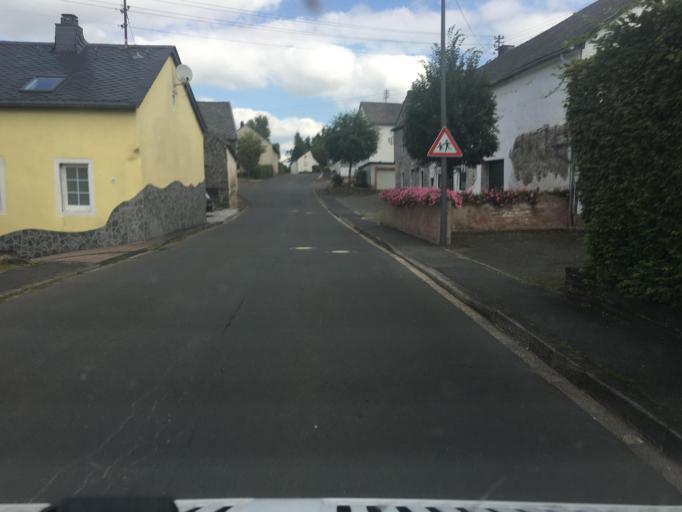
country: DE
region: Rheinland-Pfalz
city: Oberehe-Stroheich
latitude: 50.2848
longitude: 6.7546
